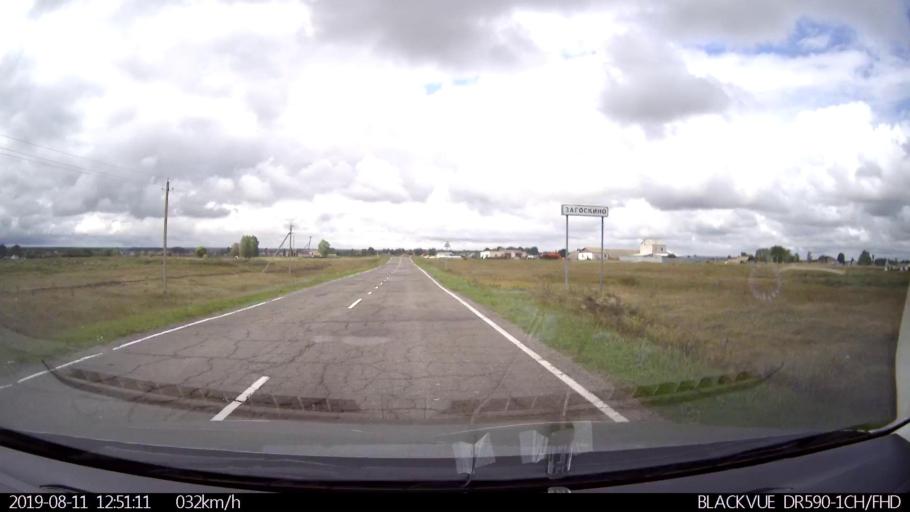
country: RU
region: Ulyanovsk
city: Ignatovka
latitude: 53.8756
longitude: 47.6648
